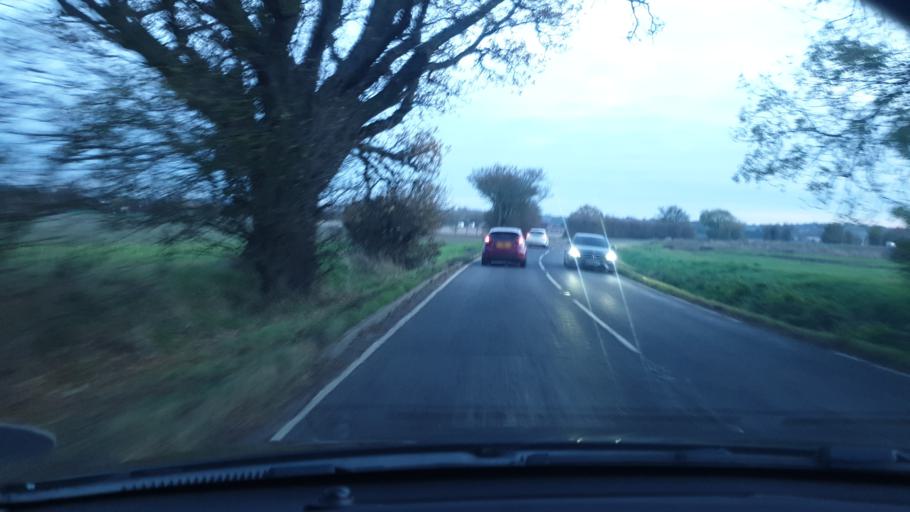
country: GB
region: England
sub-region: Essex
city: Little Clacton
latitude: 51.8765
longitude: 1.1726
